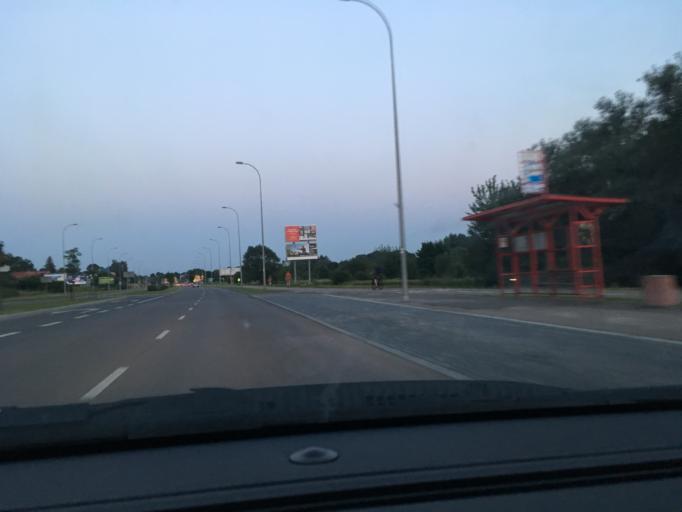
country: PL
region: Podlasie
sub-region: Bialystok
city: Bialystok
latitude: 53.1232
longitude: 23.1873
